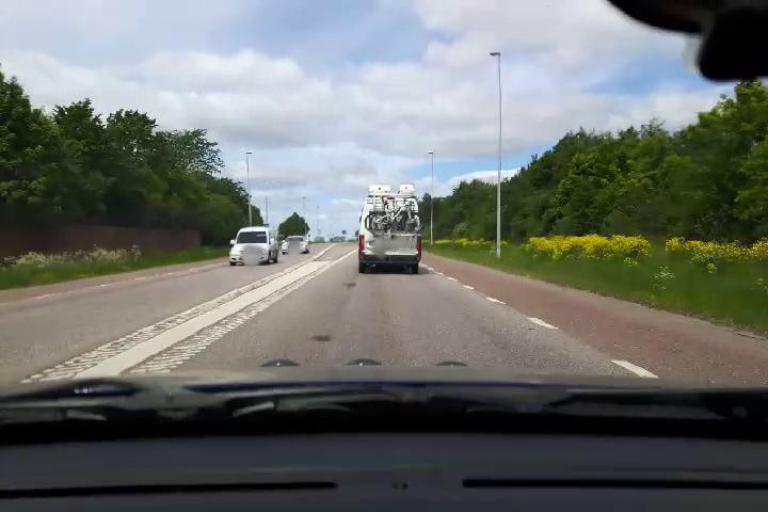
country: SE
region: Uppsala
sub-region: Uppsala Kommun
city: Gamla Uppsala
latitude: 59.8842
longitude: 17.6201
